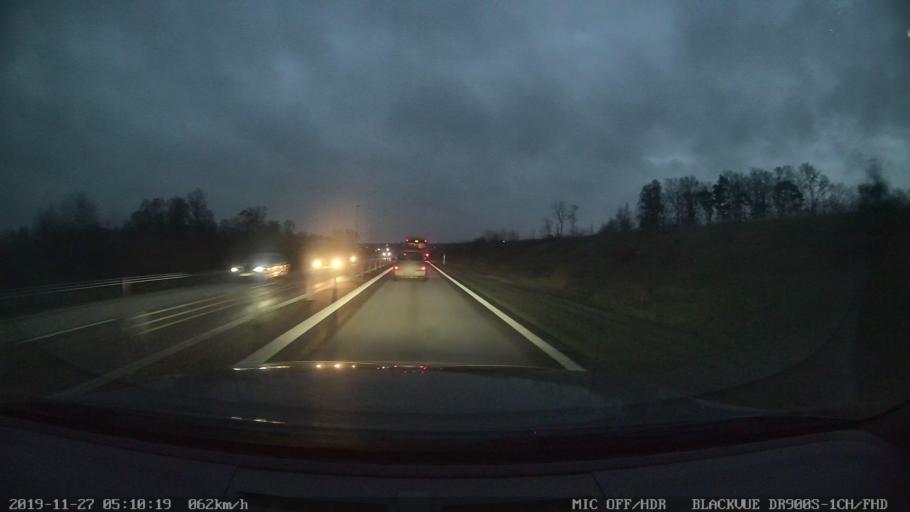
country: SE
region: Skane
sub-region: Helsingborg
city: Helsingborg
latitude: 56.1023
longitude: 12.6638
